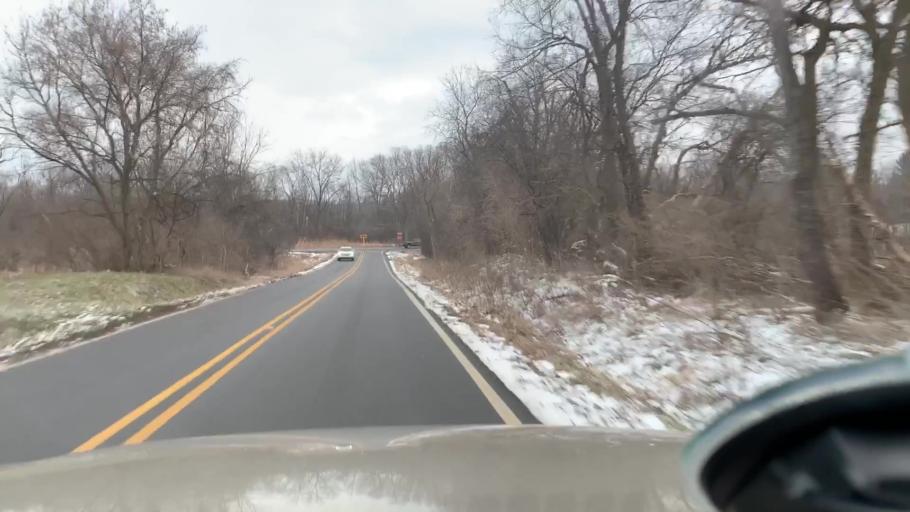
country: US
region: Michigan
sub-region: Jackson County
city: Spring Arbor
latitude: 42.2001
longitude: -84.5226
